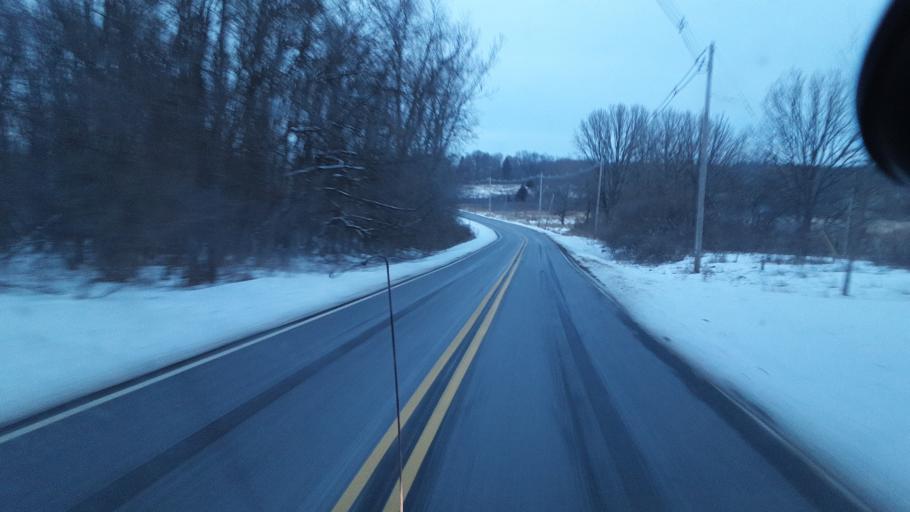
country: US
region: Michigan
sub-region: Jackson County
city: Grass Lake
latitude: 42.3071
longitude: -84.2099
